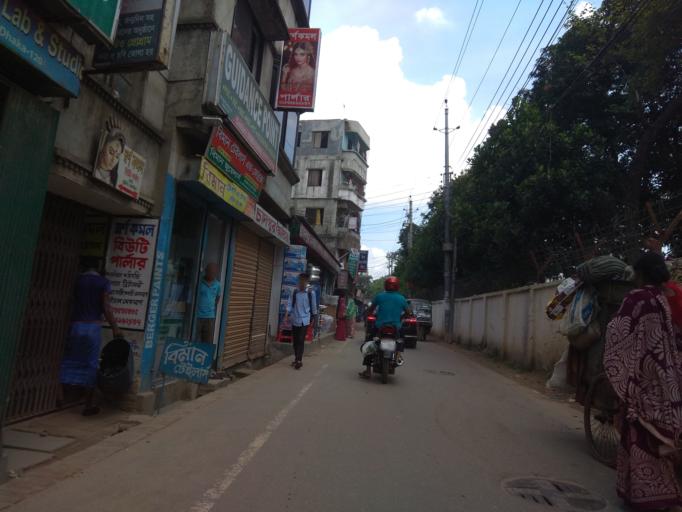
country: BD
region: Dhaka
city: Tungi
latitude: 23.8282
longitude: 90.3925
